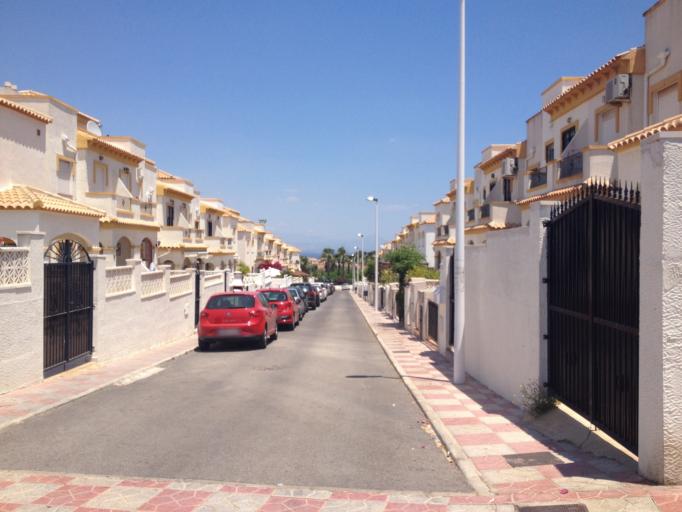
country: ES
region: Valencia
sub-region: Provincia de Alicante
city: Santa Pola
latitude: 38.2276
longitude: -0.5247
